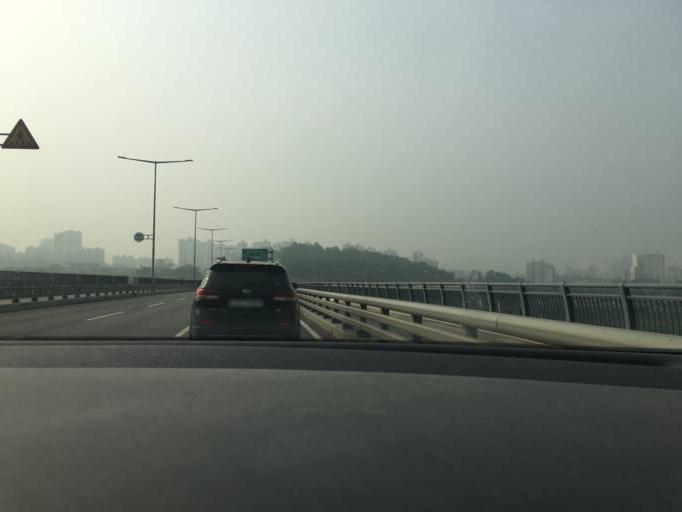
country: KR
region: Gyeonggi-do
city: Guri-si
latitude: 37.5682
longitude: 127.1325
